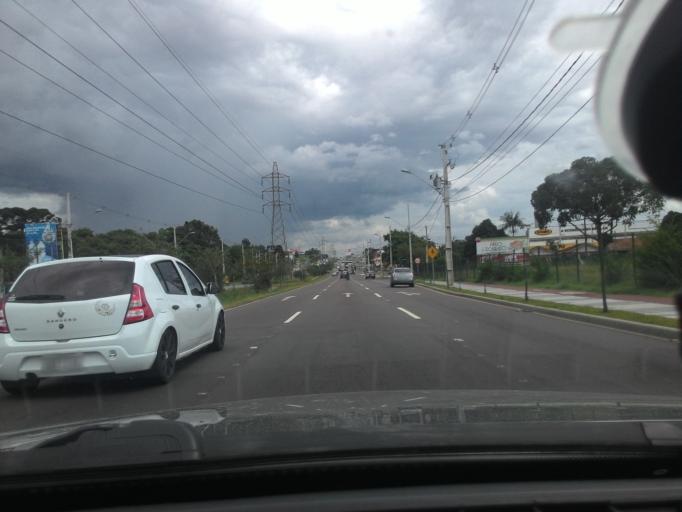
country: BR
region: Parana
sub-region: Pinhais
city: Pinhais
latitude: -25.4795
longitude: -49.2241
